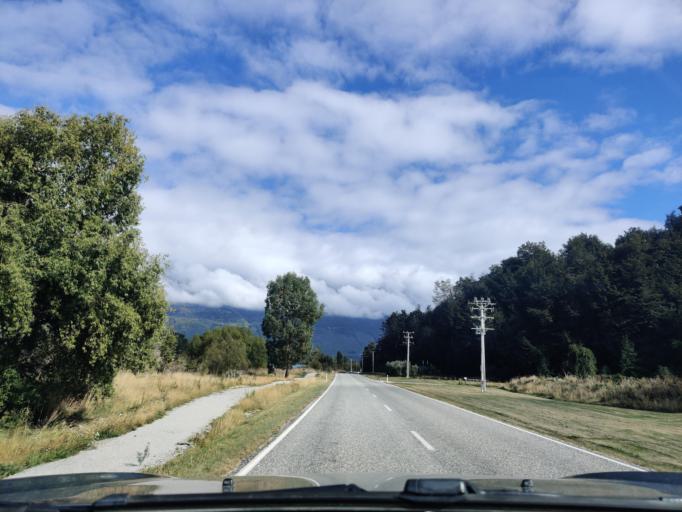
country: NZ
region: Otago
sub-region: Queenstown-Lakes District
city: Queenstown
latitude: -44.8589
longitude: 168.3975
